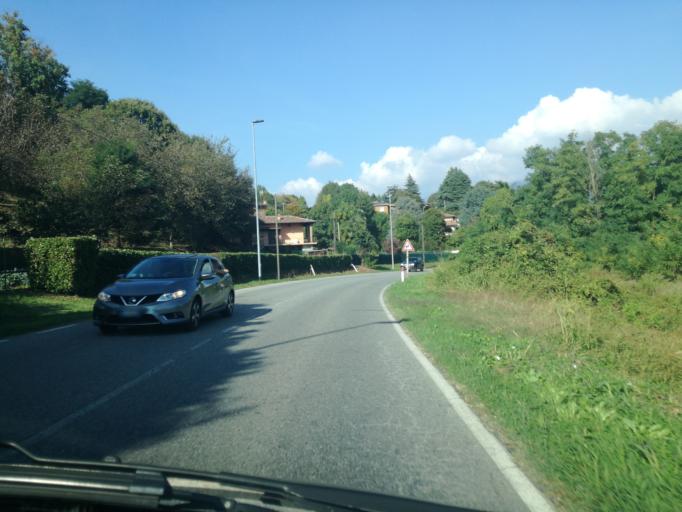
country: IT
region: Lombardy
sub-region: Provincia di Lecco
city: Brivio
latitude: 45.7346
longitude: 9.4439
